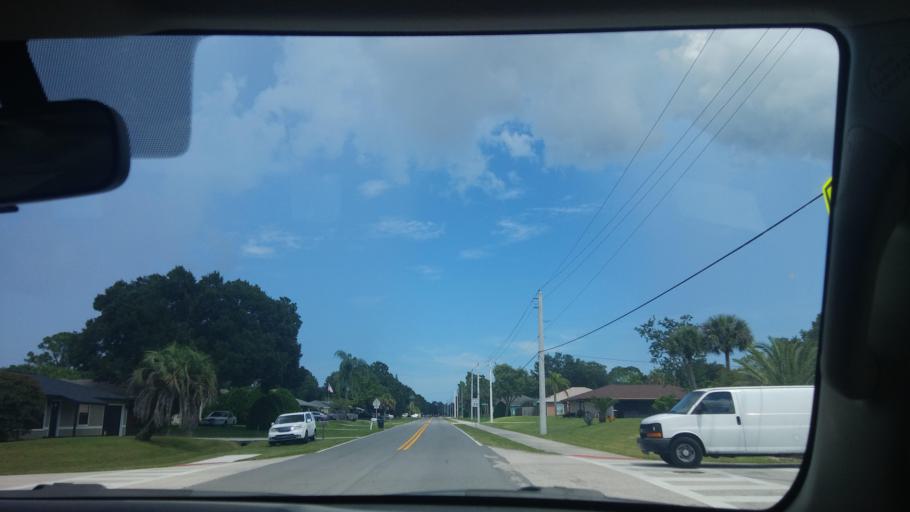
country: US
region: Florida
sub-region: Brevard County
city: June Park
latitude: 28.0110
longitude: -80.6709
